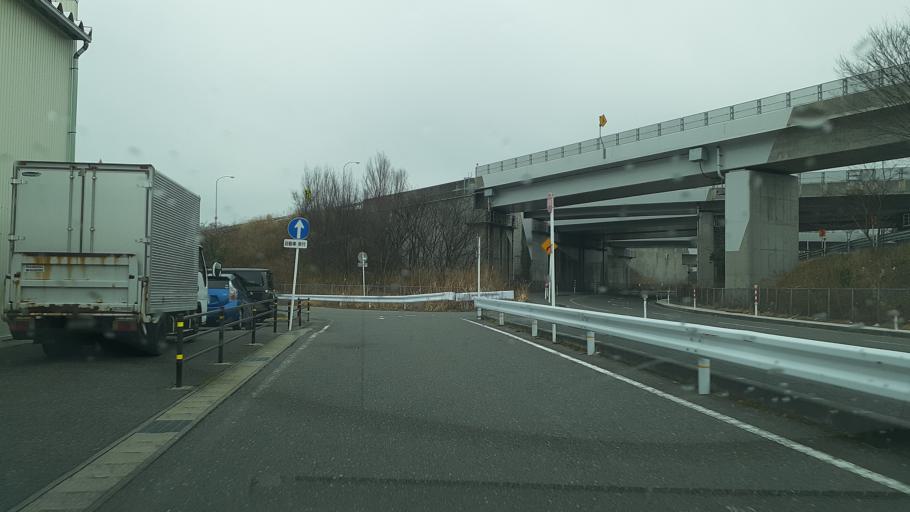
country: JP
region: Niigata
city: Niigata-shi
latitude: 37.8731
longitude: 139.0418
